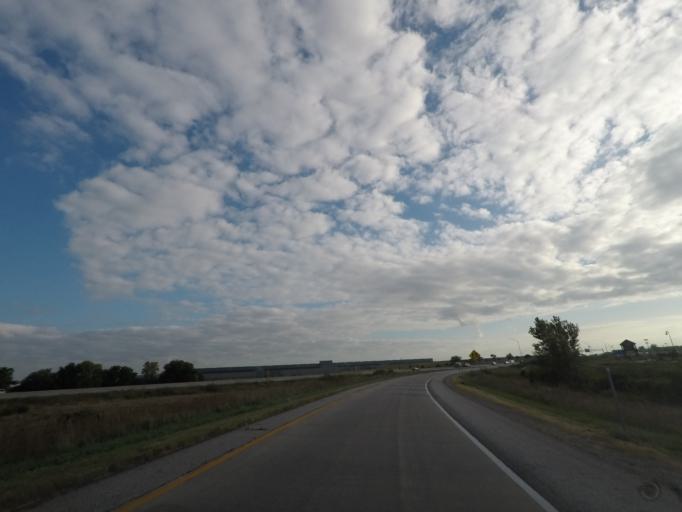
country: US
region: Iowa
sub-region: Polk County
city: Altoona
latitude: 41.6598
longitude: -93.5179
